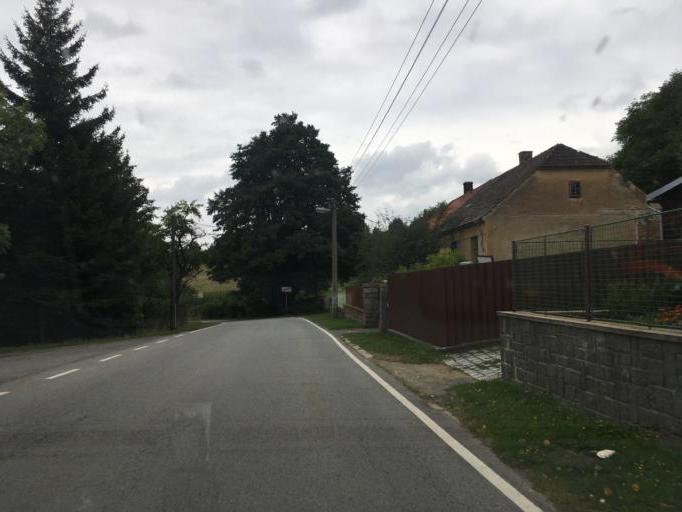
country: CZ
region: Vysocina
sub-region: Okres Jihlava
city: Telc
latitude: 49.2212
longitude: 15.4219
